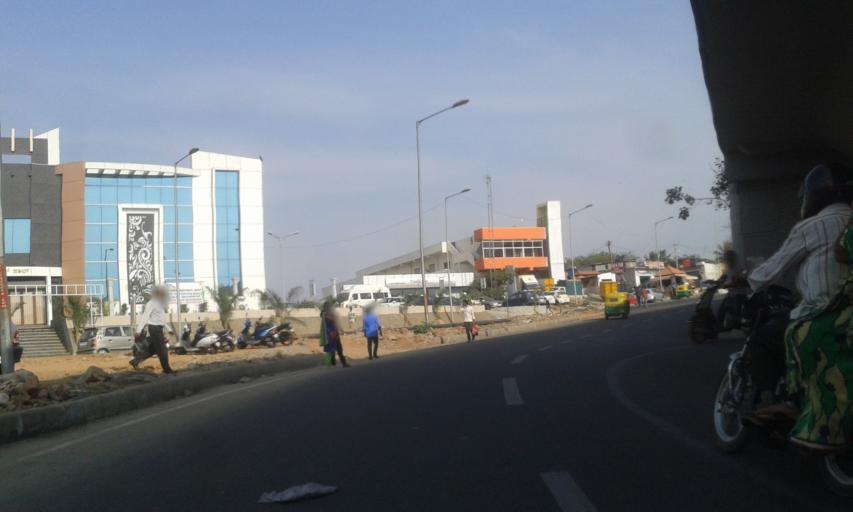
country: IN
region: Karnataka
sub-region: Bangalore Urban
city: Bangalore
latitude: 12.9452
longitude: 77.5292
